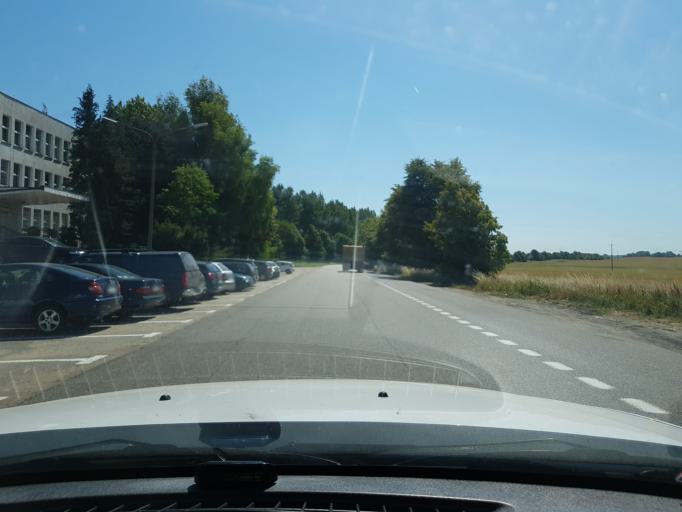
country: PL
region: West Pomeranian Voivodeship
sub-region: Powiat koszalinski
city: Mielno
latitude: 54.2125
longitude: 16.0735
